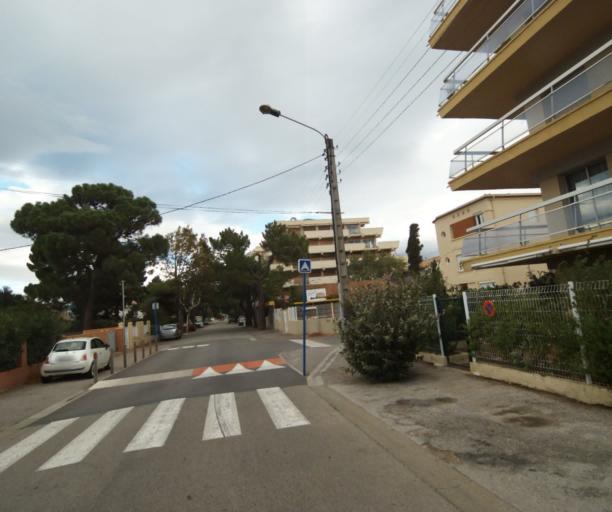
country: FR
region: Languedoc-Roussillon
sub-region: Departement des Pyrenees-Orientales
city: Argelers
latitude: 42.5582
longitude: 3.0459
